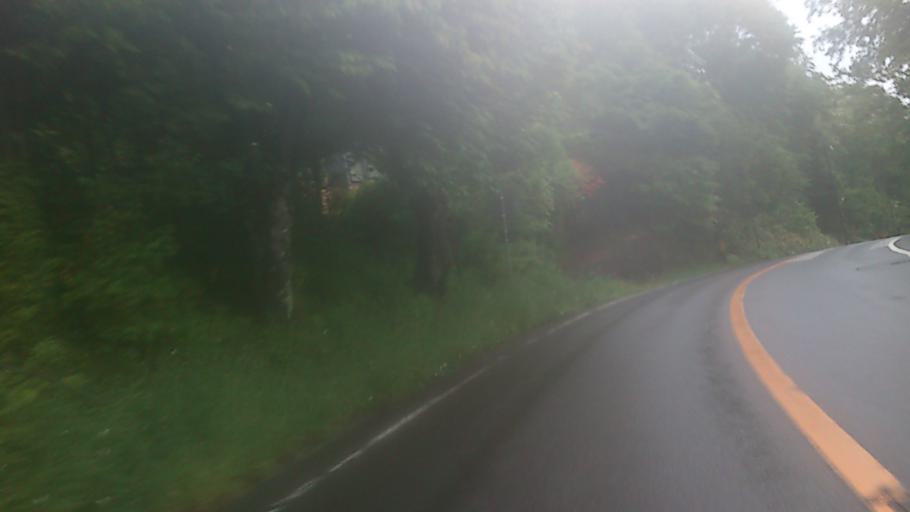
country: JP
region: Hokkaido
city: Shiraoi
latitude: 42.7768
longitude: 141.4027
